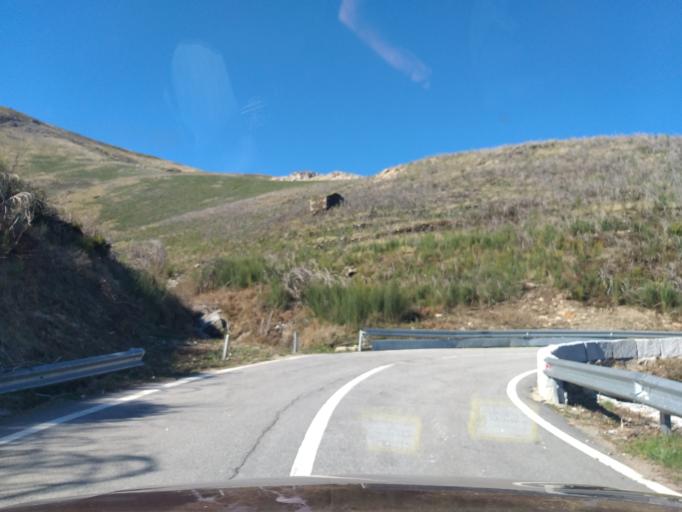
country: PT
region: Guarda
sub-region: Manteigas
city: Manteigas
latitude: 40.4702
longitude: -7.5208
